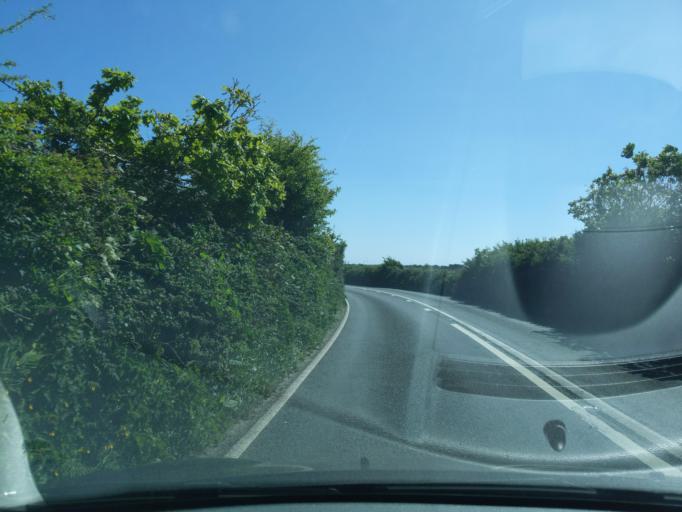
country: GB
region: England
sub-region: Cornwall
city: Wendron
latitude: 50.1158
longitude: -5.2445
